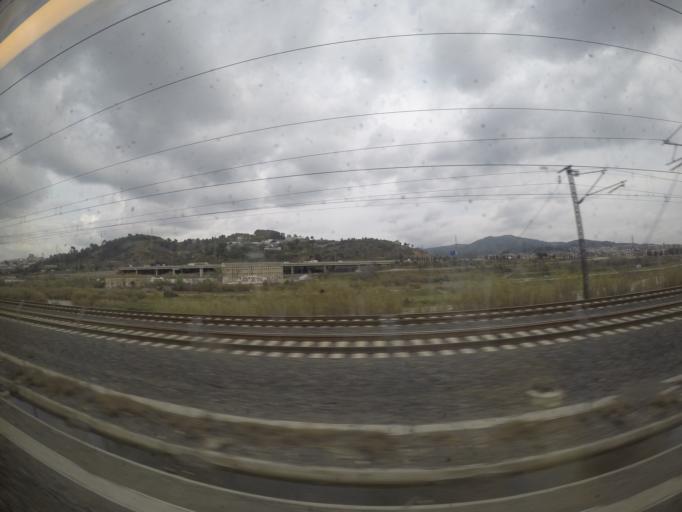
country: ES
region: Catalonia
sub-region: Provincia de Barcelona
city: Palleja
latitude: 41.4217
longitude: 2.0039
